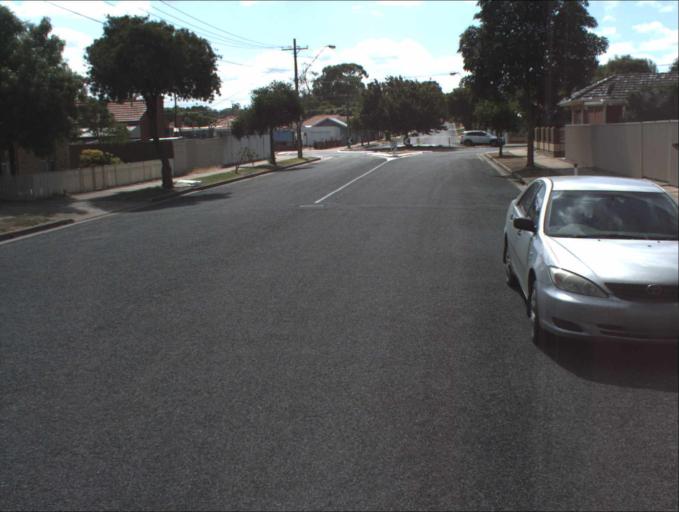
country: AU
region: South Australia
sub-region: Port Adelaide Enfield
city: Blair Athol
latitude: -34.8575
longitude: 138.5952
